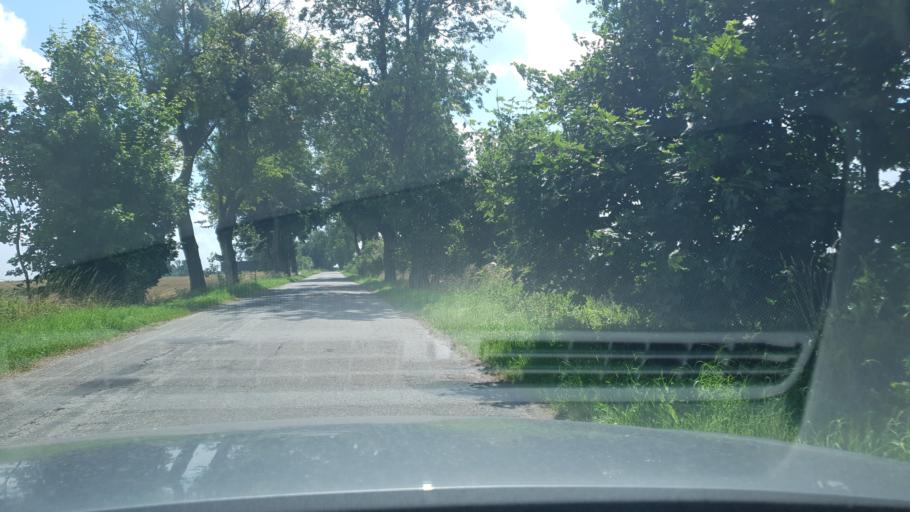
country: PL
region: Kujawsko-Pomorskie
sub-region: Powiat wabrzeski
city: Pluznica
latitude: 53.3666
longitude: 18.8063
